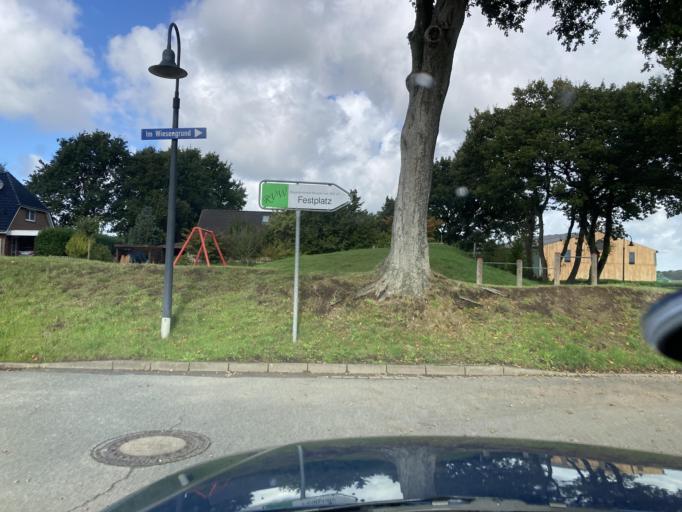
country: DE
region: Schleswig-Holstein
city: Wesseln
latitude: 54.2107
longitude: 9.0784
